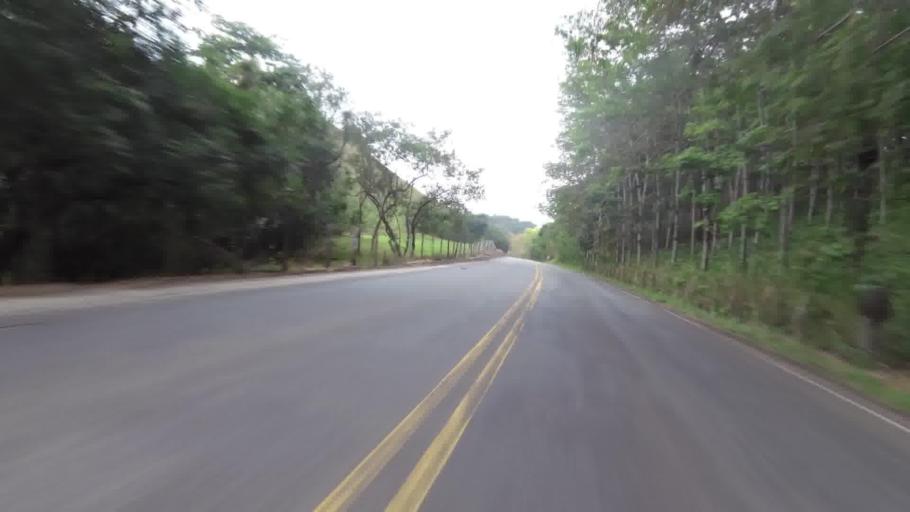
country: BR
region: Espirito Santo
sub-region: Alfredo Chaves
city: Alfredo Chaves
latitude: -20.6776
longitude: -40.7093
